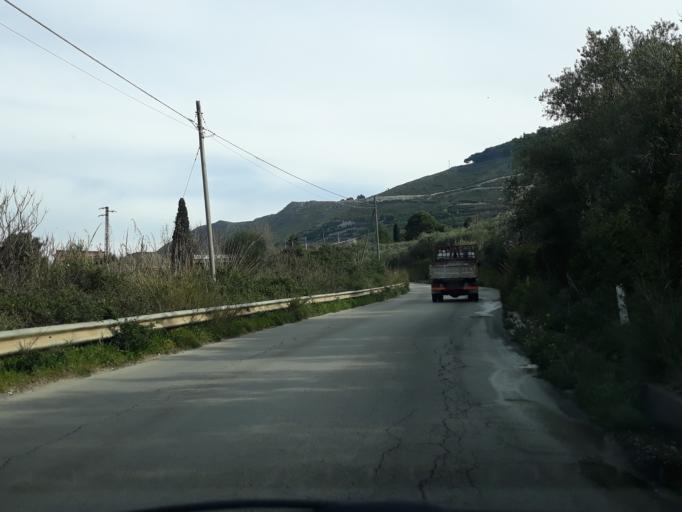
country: IT
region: Sicily
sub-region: Palermo
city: Piano Maglio-Blandino
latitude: 38.0419
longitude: 13.3188
